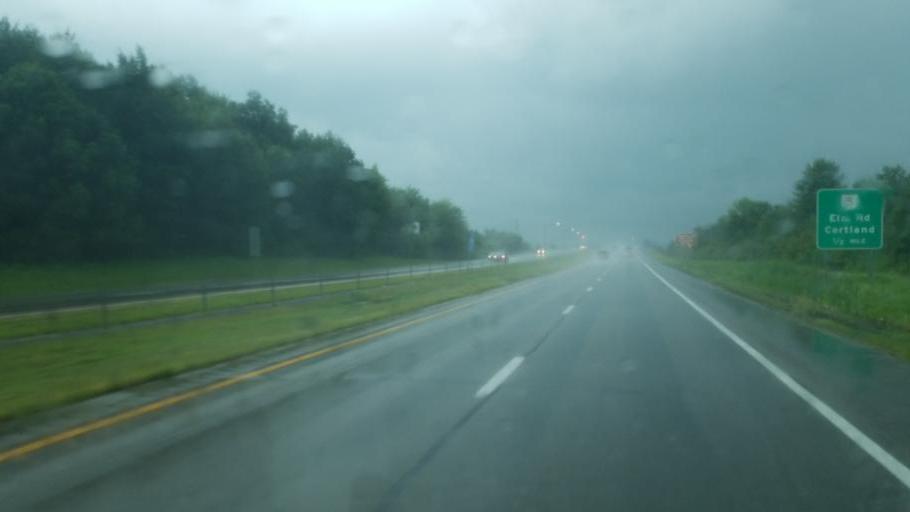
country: US
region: Ohio
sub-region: Trumbull County
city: Morgandale
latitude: 41.2757
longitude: -80.7867
